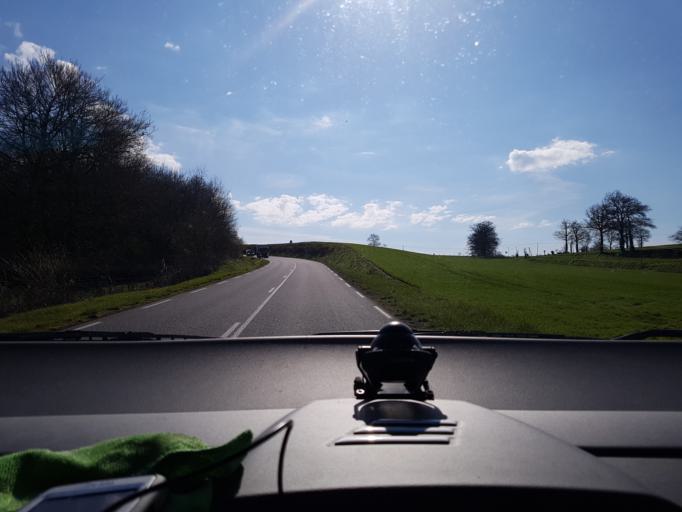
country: FR
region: Midi-Pyrenees
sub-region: Departement de l'Aveyron
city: Colombies
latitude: 44.4009
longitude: 2.3462
